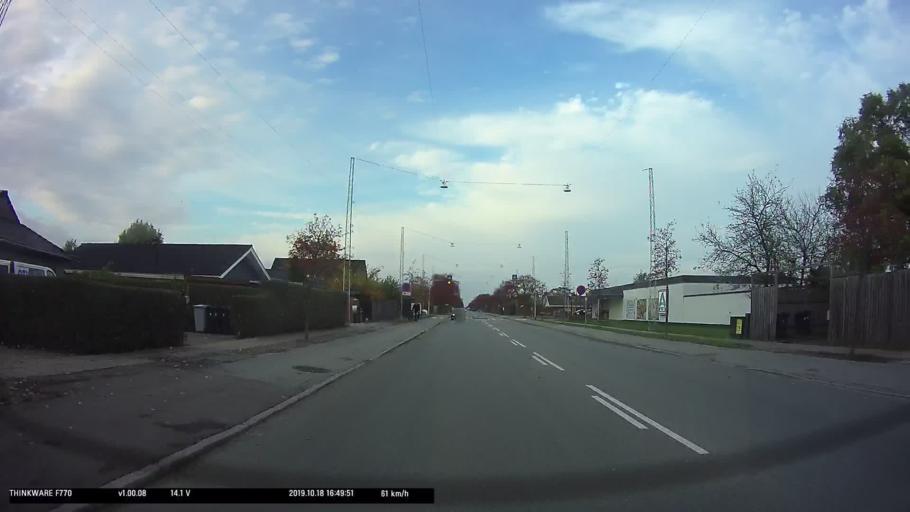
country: DK
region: Capital Region
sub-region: Tarnby Kommune
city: Tarnby
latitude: 55.5984
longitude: 12.5825
